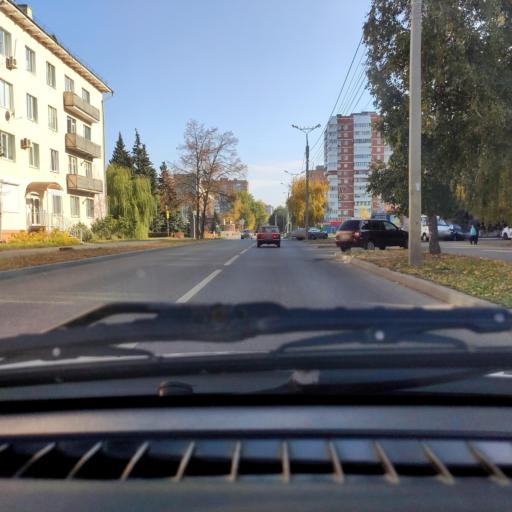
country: RU
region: Samara
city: Tol'yatti
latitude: 53.5061
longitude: 49.4178
